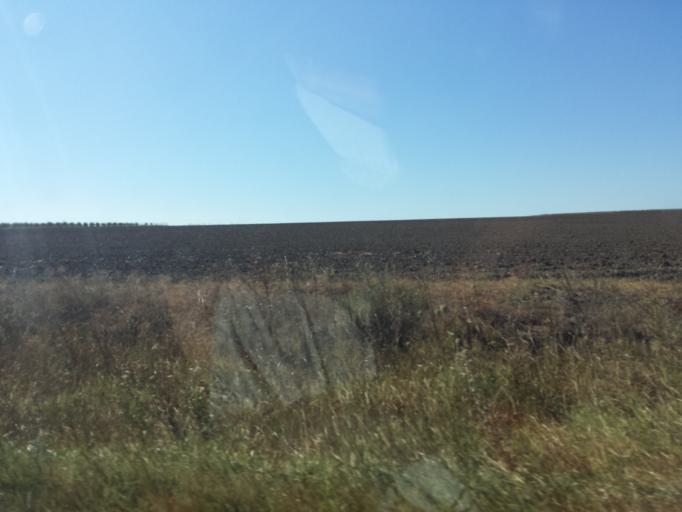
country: RO
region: Tulcea
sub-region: Comuna Frecatei
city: Cataloi
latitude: 45.1074
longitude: 28.7441
